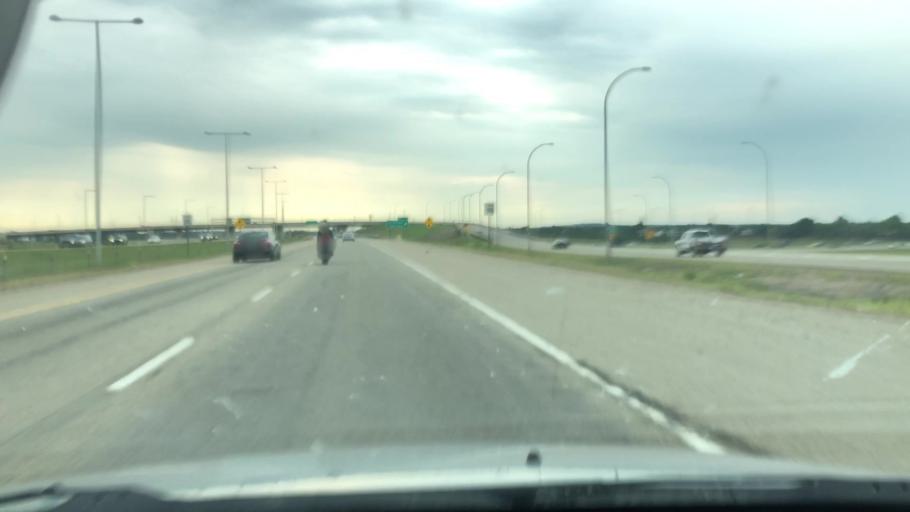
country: CA
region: Alberta
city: Beaumont
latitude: 53.4378
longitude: -113.4855
